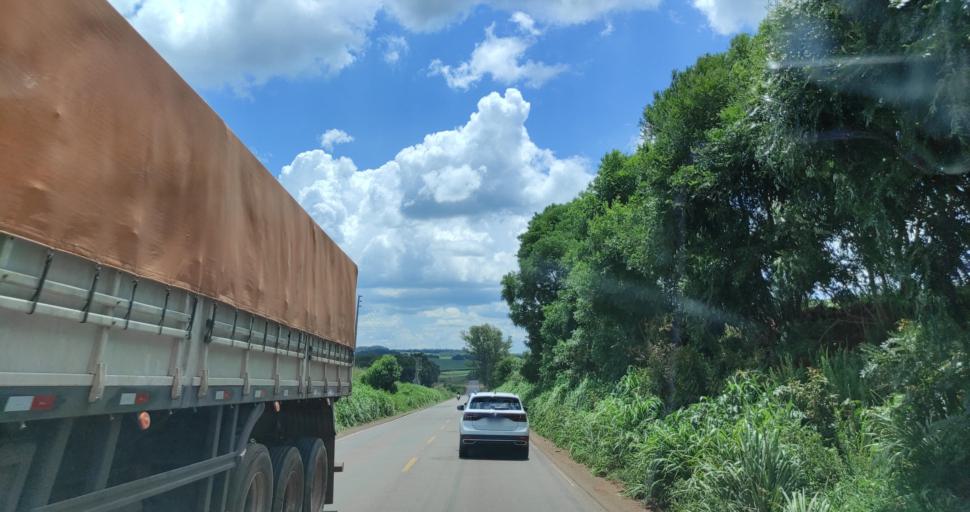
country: BR
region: Santa Catarina
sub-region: Xanxere
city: Xanxere
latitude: -26.7599
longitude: -52.4037
